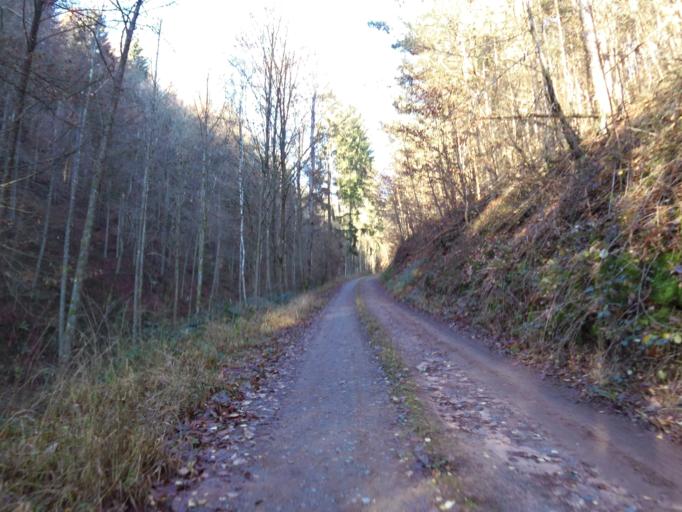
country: DE
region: Rheinland-Pfalz
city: Altleiningen
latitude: 49.4687
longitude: 8.1093
